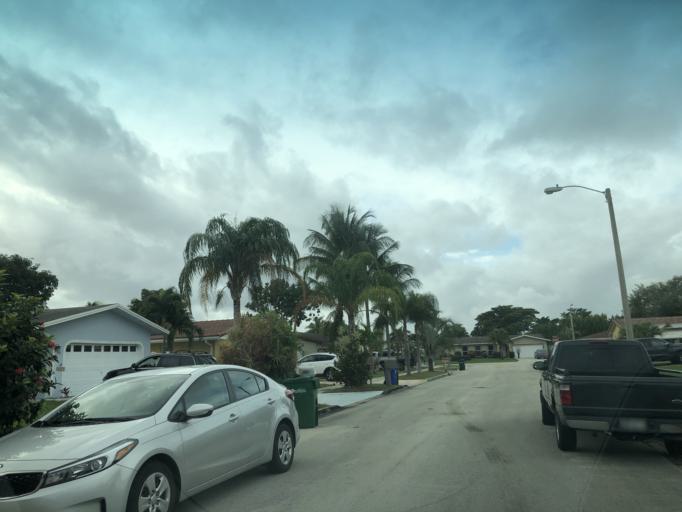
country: US
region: Florida
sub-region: Broward County
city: North Lauderdale
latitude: 26.2417
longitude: -80.2324
